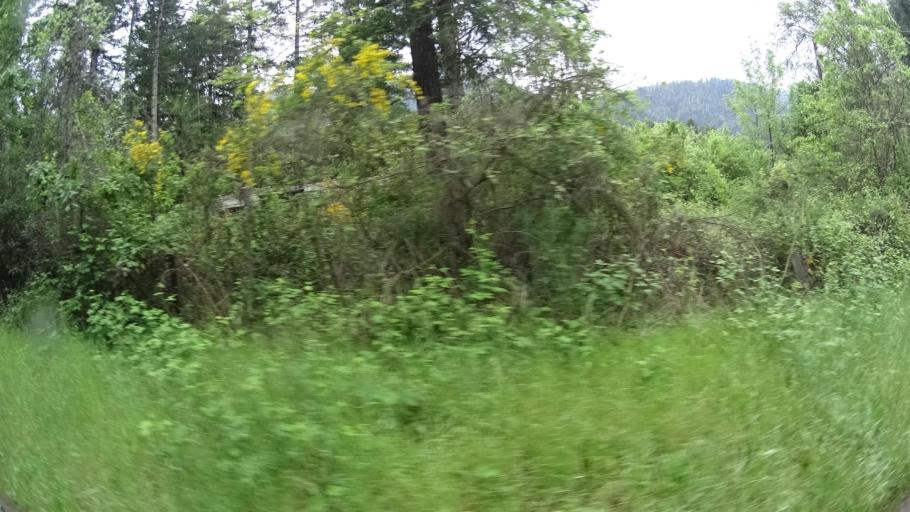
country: US
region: California
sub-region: Humboldt County
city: Willow Creek
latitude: 41.0473
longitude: -123.6633
